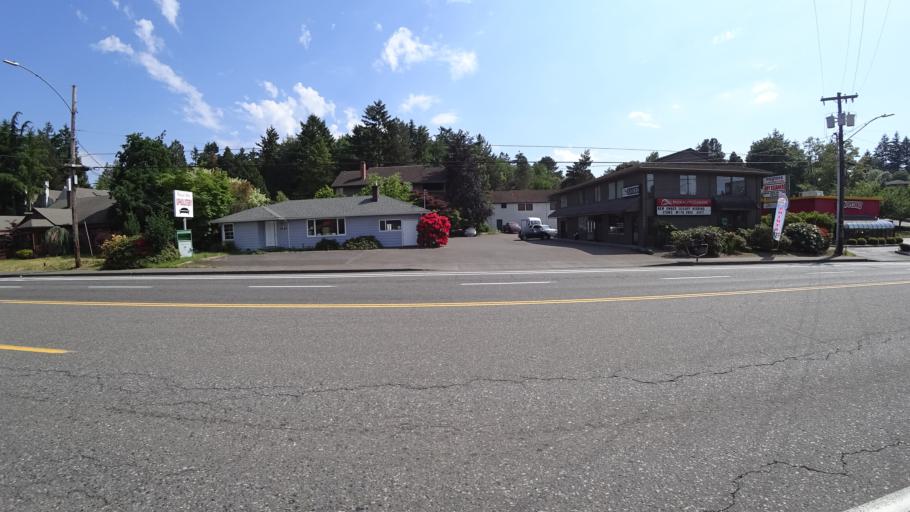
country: US
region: Oregon
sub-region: Washington County
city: Raleigh Hills
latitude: 45.4871
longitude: -122.7308
